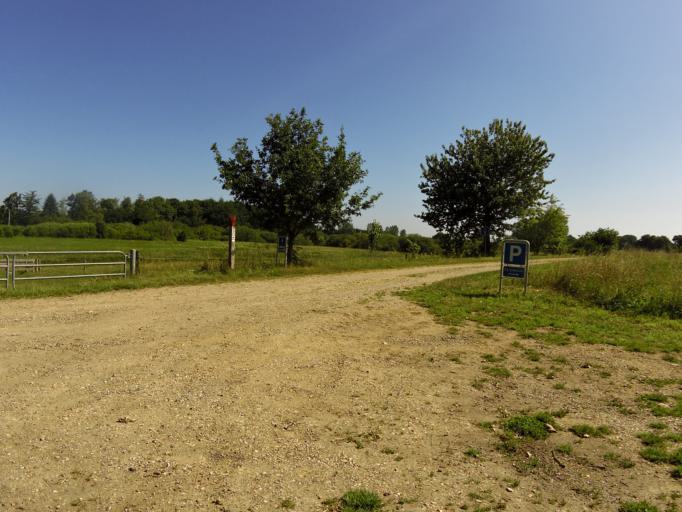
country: DK
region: South Denmark
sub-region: Vejen Kommune
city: Vejen
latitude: 55.4345
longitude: 9.1096
